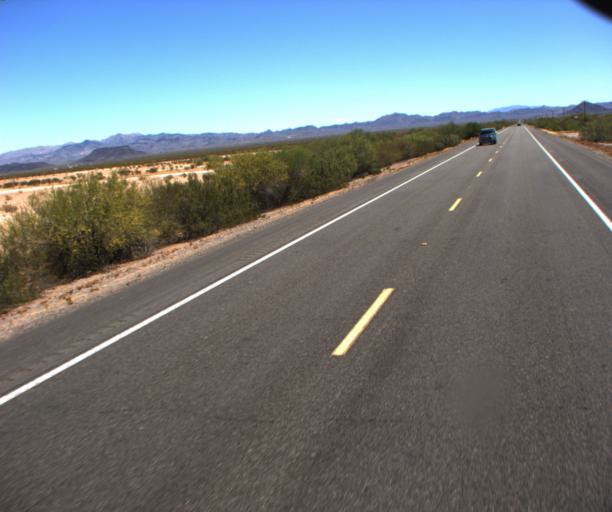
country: US
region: Arizona
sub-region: La Paz County
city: Salome
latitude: 33.7024
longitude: -113.8464
